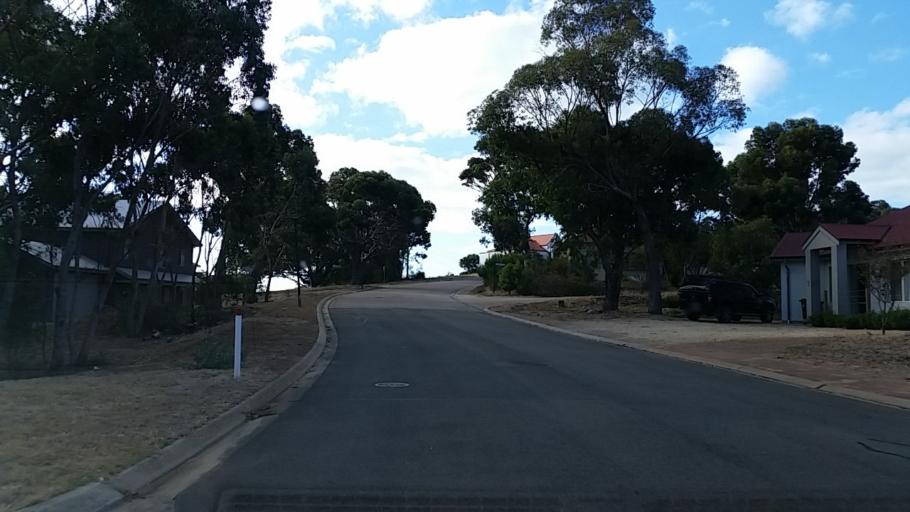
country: AU
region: South Australia
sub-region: Yankalilla
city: Normanville
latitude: -35.5063
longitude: 138.2461
